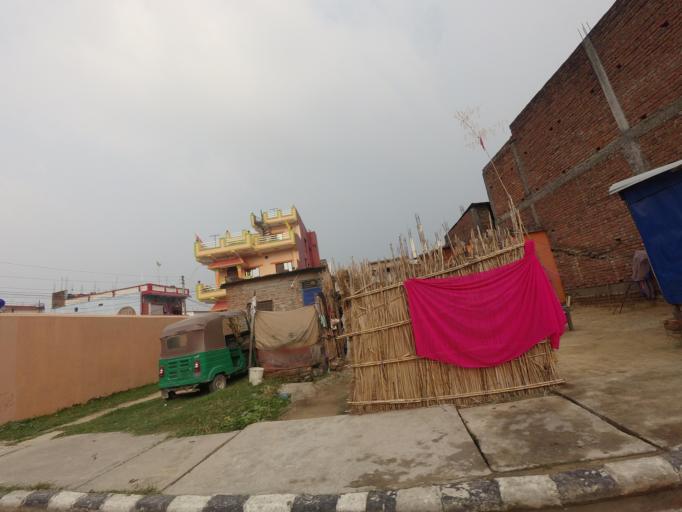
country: NP
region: Western Region
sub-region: Lumbini Zone
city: Bhairahawa
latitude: 27.5031
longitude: 83.4489
